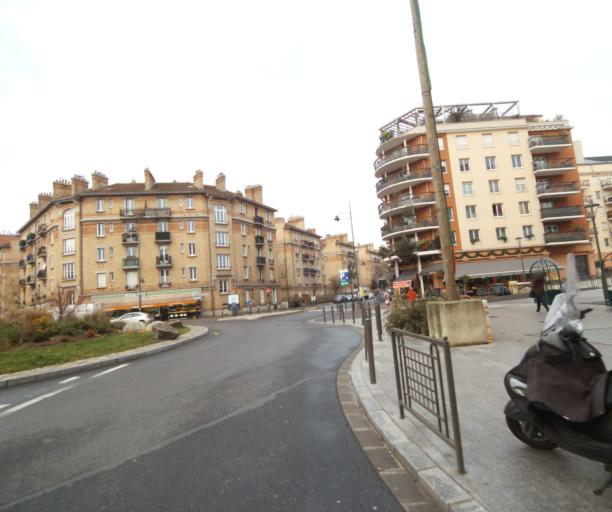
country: FR
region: Ile-de-France
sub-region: Departement des Hauts-de-Seine
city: Saint-Cloud
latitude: 48.8631
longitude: 2.2101
